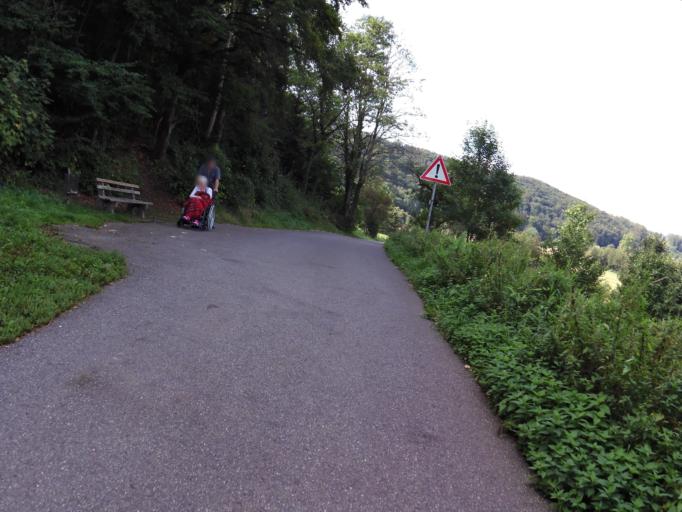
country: DE
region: Baden-Wuerttemberg
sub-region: Karlsruhe Region
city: Horb am Neckar
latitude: 48.4461
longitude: 8.7180
